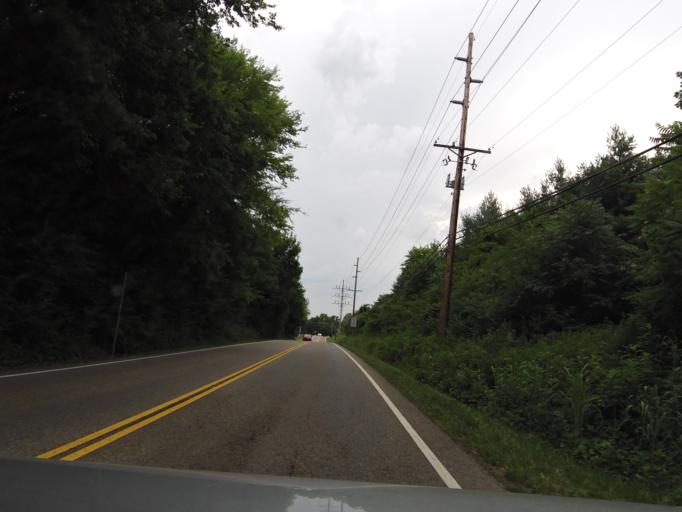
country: US
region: Tennessee
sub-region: Knox County
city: Farragut
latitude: 35.8638
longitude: -84.1424
